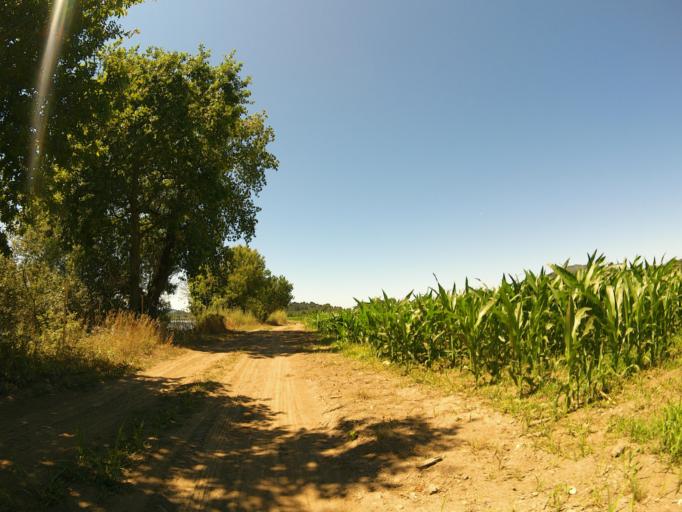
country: PT
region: Viana do Castelo
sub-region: Viana do Castelo
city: Darque
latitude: 41.7160
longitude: -8.7078
